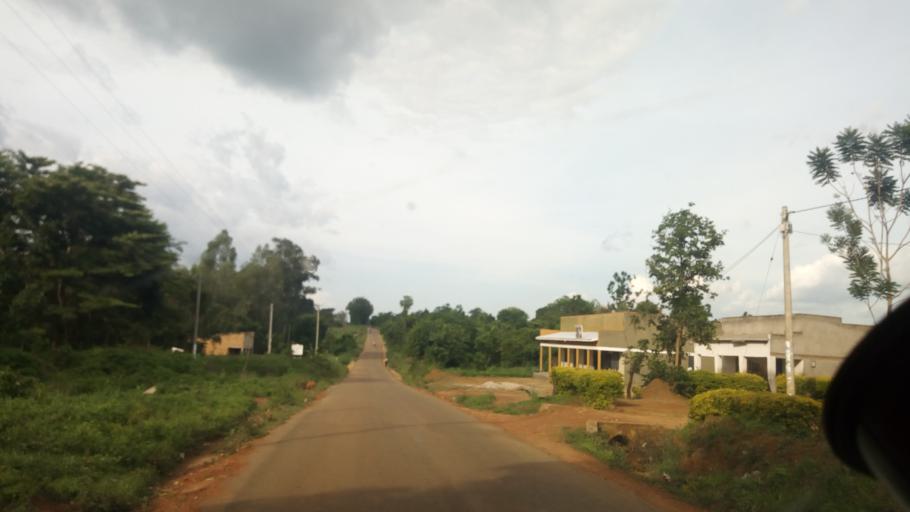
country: UG
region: Northern Region
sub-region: Lira District
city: Lira
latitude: 2.2529
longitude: 32.8415
